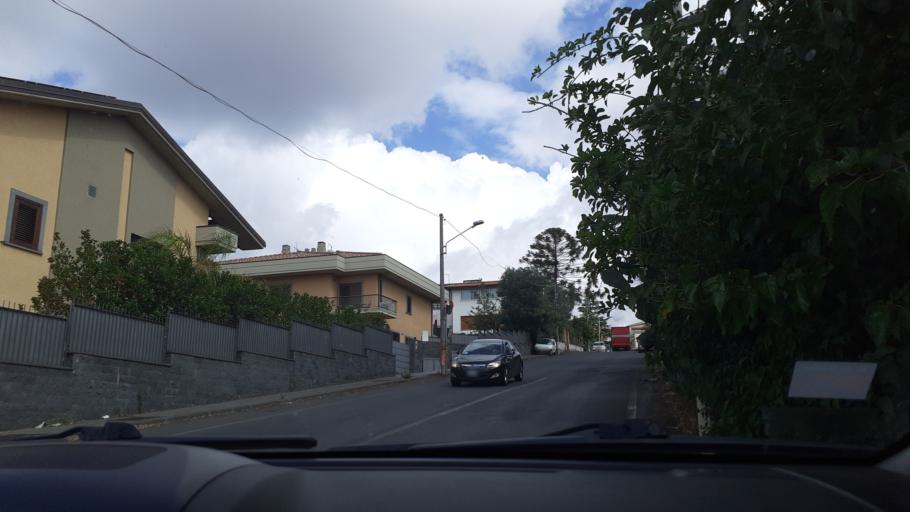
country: IT
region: Sicily
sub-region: Catania
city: Carrubazza-Motta
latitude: 37.5609
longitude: 15.1053
